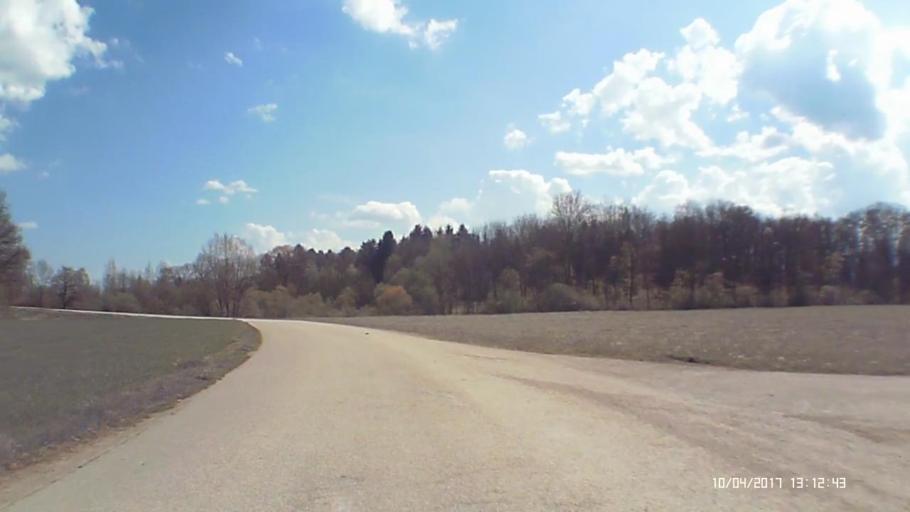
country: DE
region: Bavaria
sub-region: Upper Bavaria
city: Chieming
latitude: 47.9065
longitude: 12.5112
